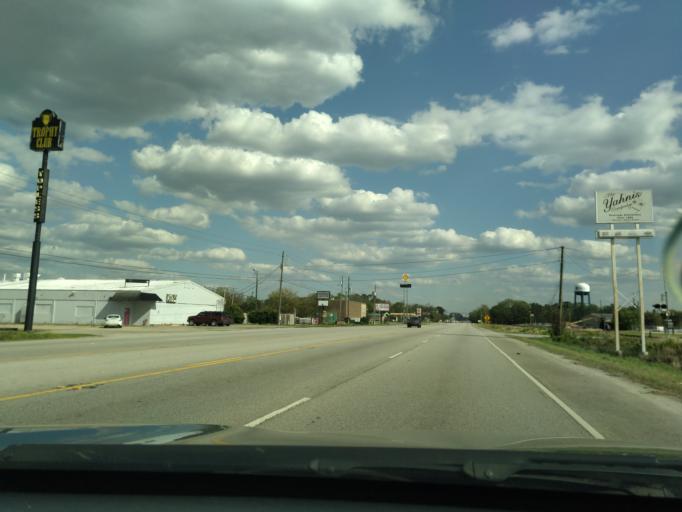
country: US
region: South Carolina
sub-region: Florence County
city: Florence
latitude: 34.2245
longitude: -79.7931
